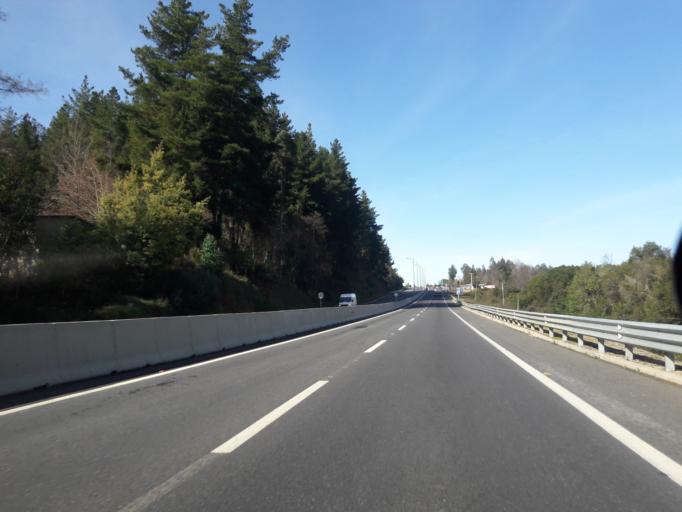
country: CL
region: Biobio
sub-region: Provincia de Concepcion
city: Chiguayante
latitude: -36.9282
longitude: -72.7679
